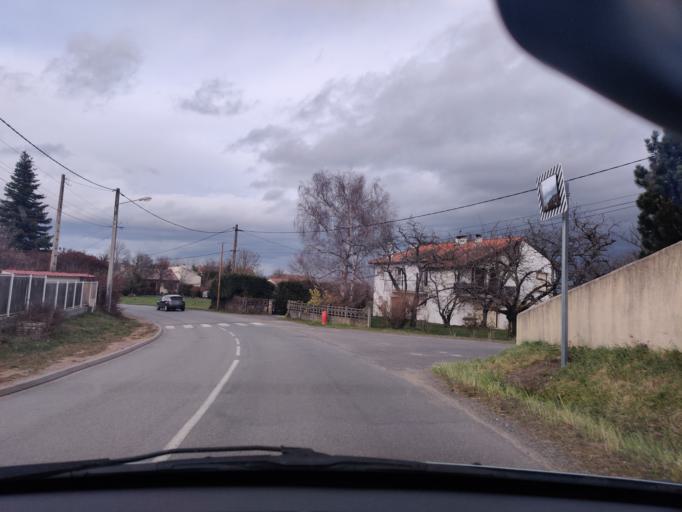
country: FR
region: Auvergne
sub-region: Departement du Puy-de-Dome
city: Saint-Bonnet-pres-Riom
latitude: 45.9309
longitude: 3.0910
